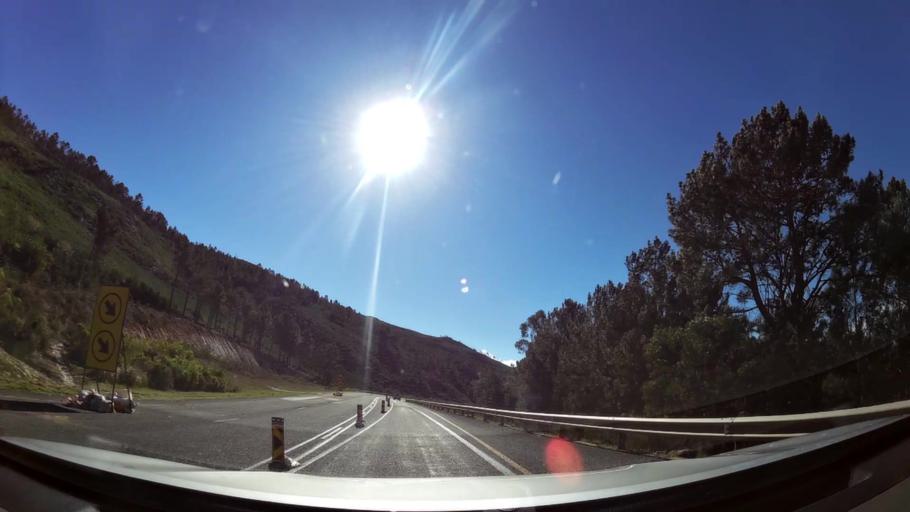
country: ZA
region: Western Cape
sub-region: Overberg District Municipality
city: Caledon
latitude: -34.2114
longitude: 19.5691
